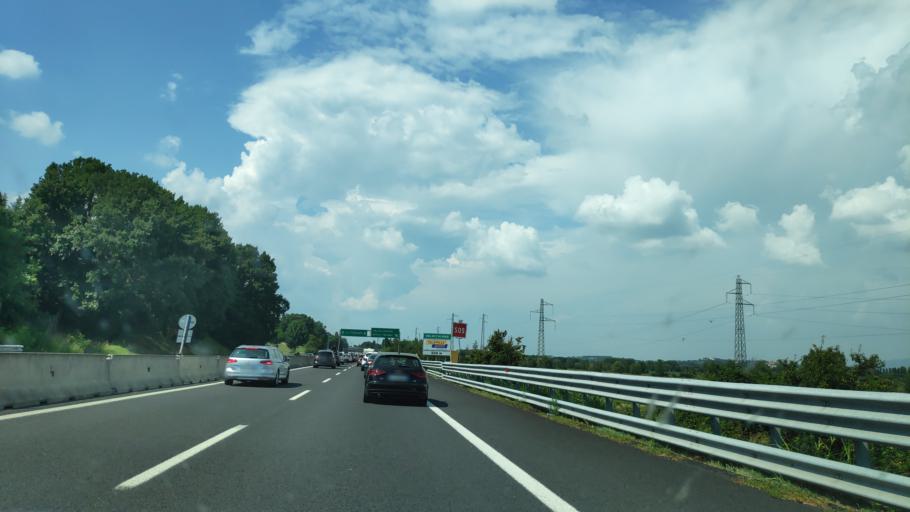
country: IT
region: Tuscany
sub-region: Provincia di Siena
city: Bettolle
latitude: 43.2073
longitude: 11.8123
